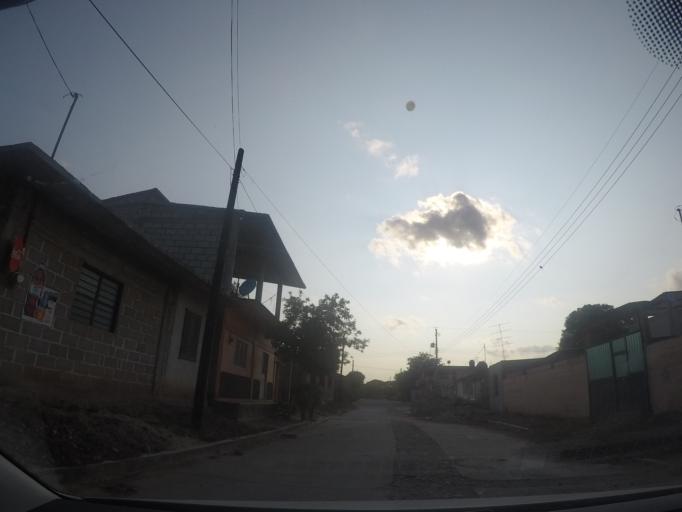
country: MX
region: Oaxaca
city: San Jeronimo Ixtepec
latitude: 16.5918
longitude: -95.1595
